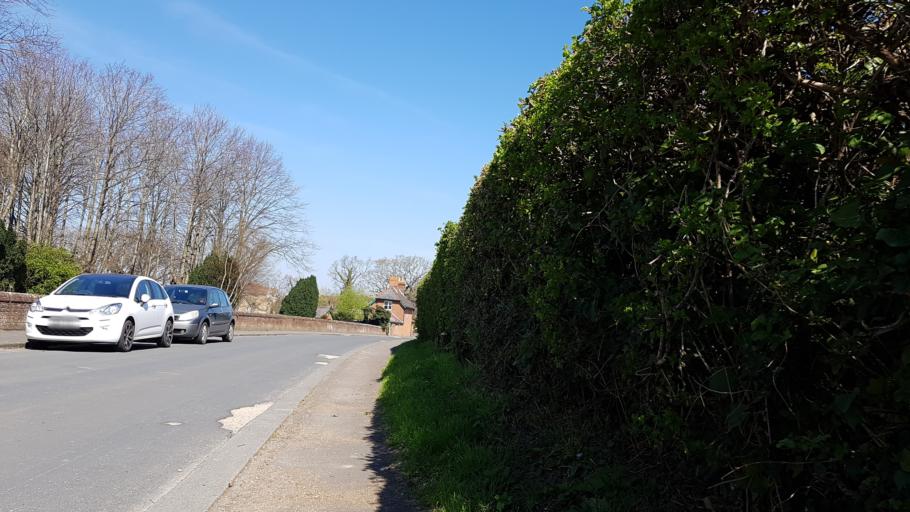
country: GB
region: England
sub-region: Isle of Wight
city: East Cowes
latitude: 50.7492
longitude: -1.2872
